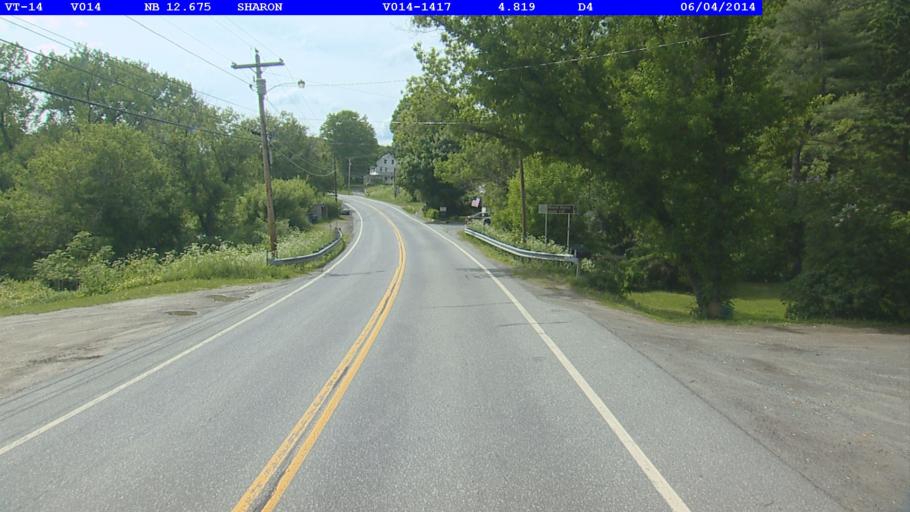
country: US
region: Vermont
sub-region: Windsor County
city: Woodstock
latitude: 43.7840
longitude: -72.4501
